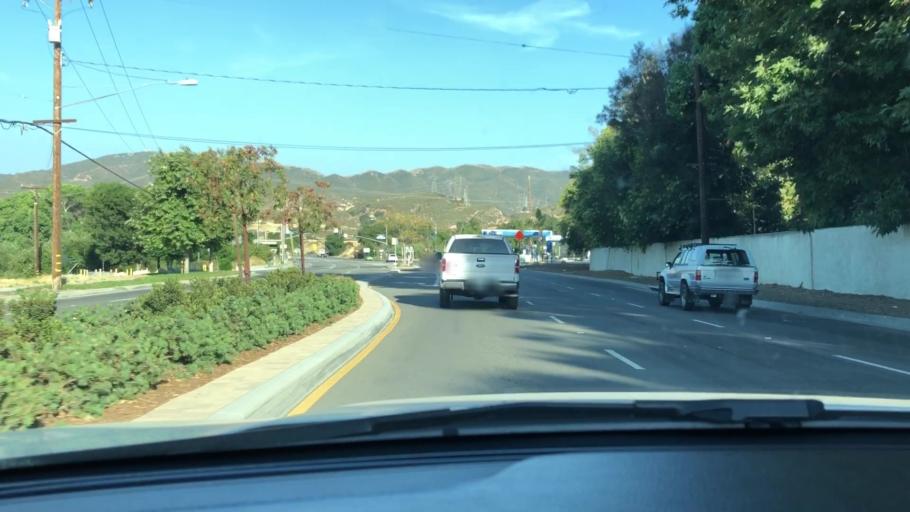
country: US
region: California
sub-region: Los Angeles County
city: Santa Clarita
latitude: 34.3669
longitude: -118.5084
